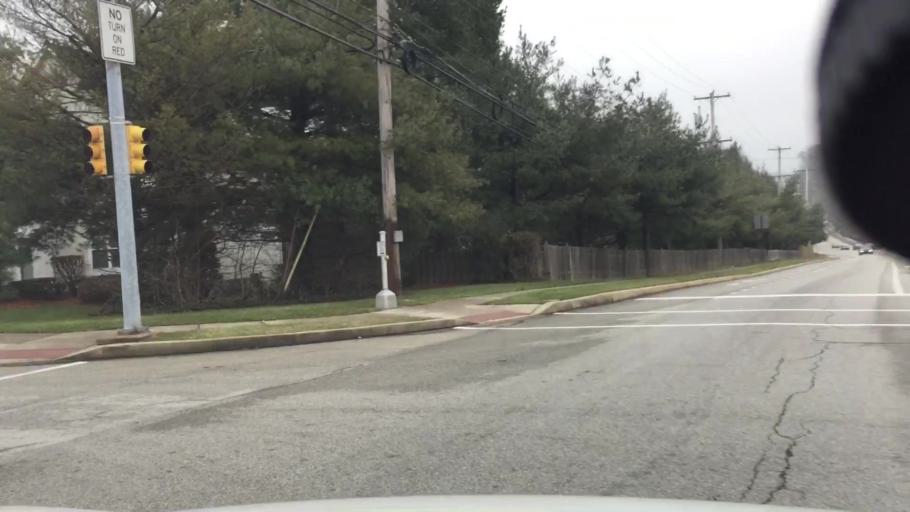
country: US
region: Pennsylvania
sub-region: Montgomery County
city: Dresher
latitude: 40.1509
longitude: -75.1834
